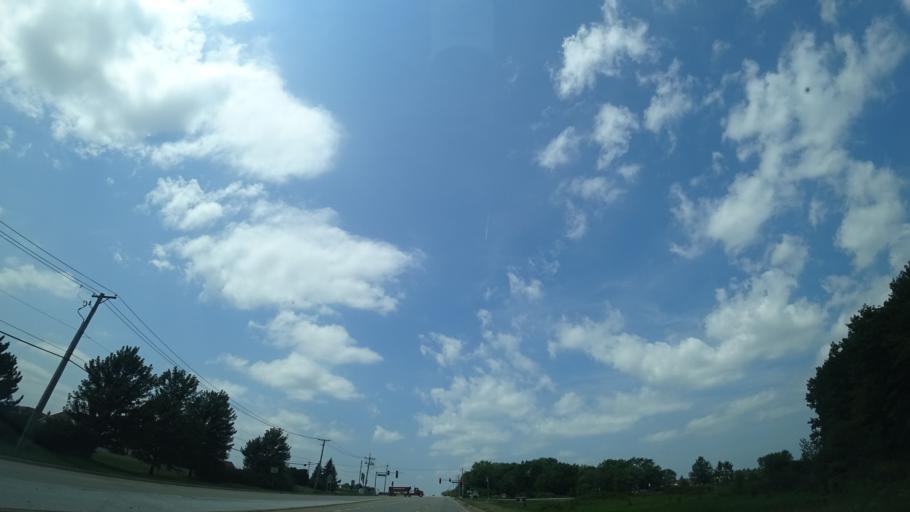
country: US
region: Illinois
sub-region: Will County
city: Frankfort Square
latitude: 41.5271
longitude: -87.7696
